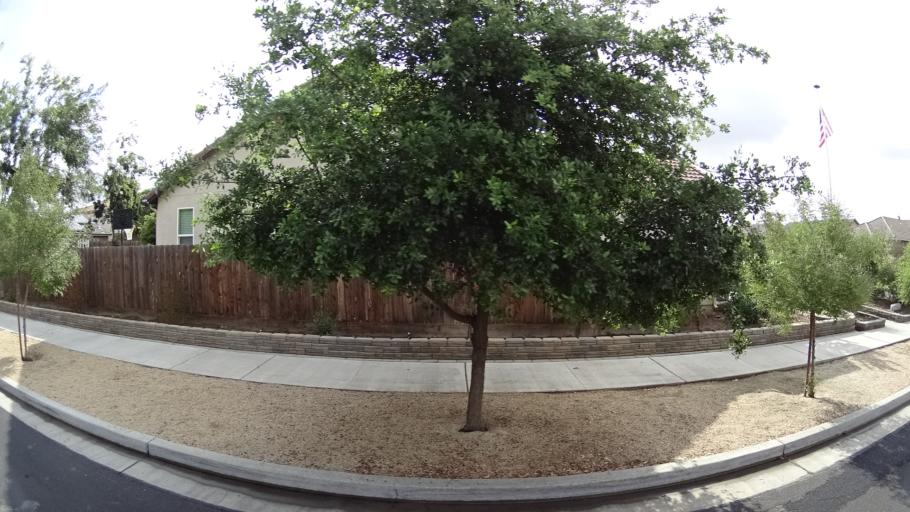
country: US
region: California
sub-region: Kings County
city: Lucerne
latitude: 36.3529
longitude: -119.6665
